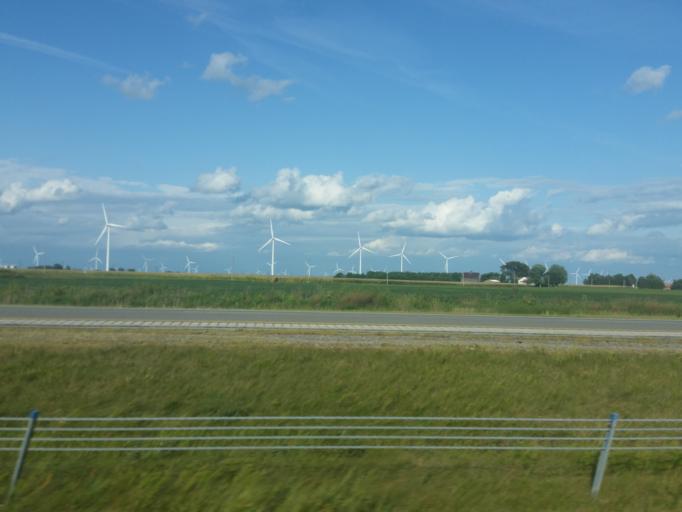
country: US
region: Indiana
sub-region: White County
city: Wolcott
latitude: 40.6339
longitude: -87.0050
